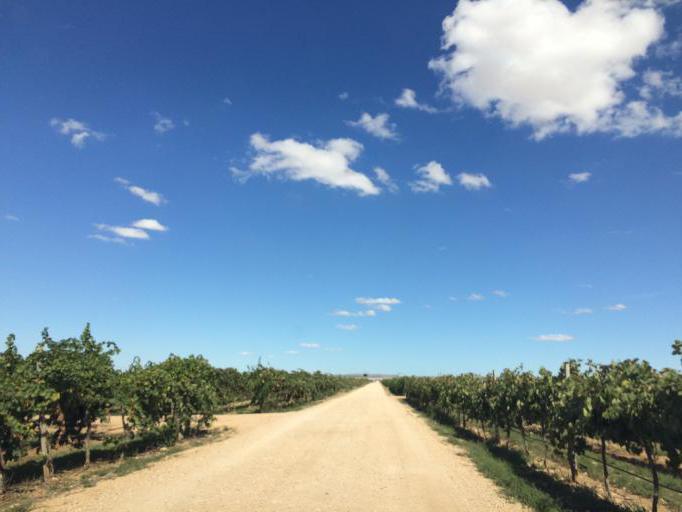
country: ES
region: Castille-La Mancha
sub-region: Provincia de Albacete
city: Albacete
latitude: 38.9312
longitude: -1.8583
